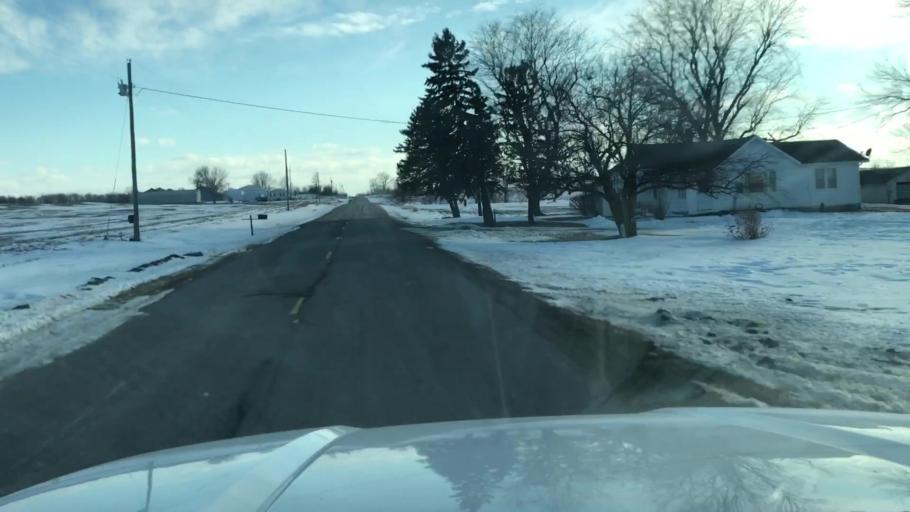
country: US
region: Missouri
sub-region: Holt County
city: Oregon
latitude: 40.1174
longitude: -95.0226
